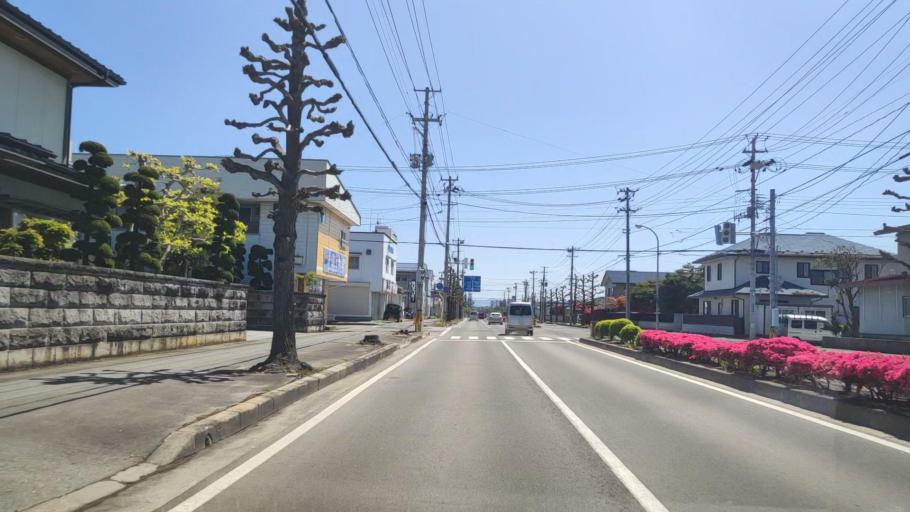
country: JP
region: Yamagata
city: Tendo
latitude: 38.3681
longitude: 140.3677
